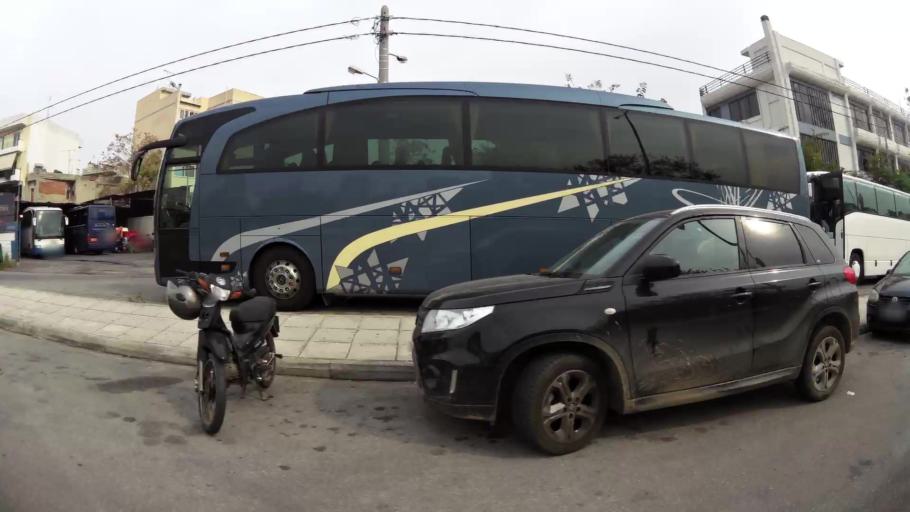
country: GR
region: Attica
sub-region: Nomarchia Athinas
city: Chaidari
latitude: 38.0133
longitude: 23.6610
